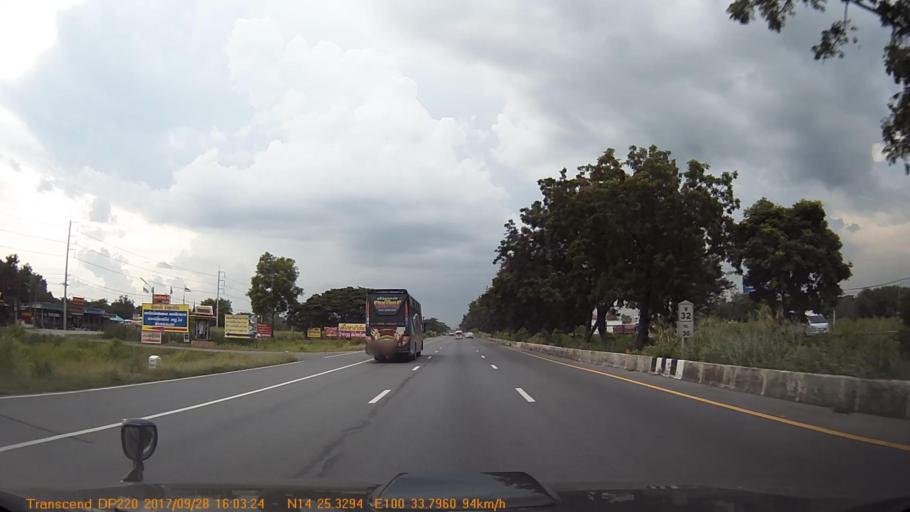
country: TH
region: Phra Nakhon Si Ayutthaya
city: Bang Pahan
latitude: 14.4225
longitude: 100.5633
